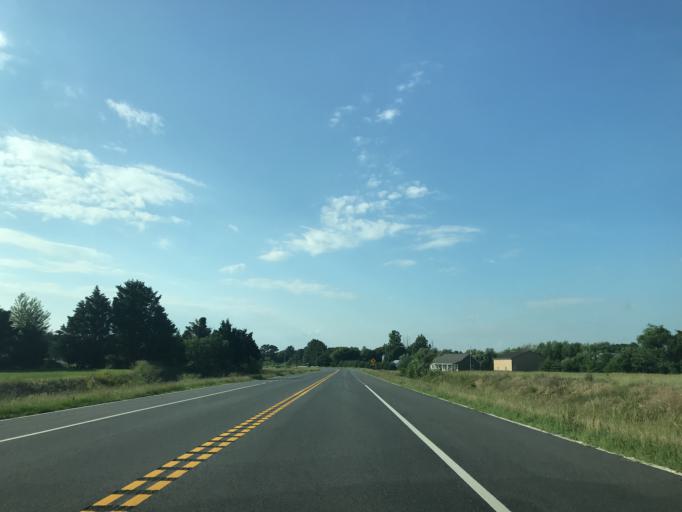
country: US
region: Maryland
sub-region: Wicomico County
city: Hebron
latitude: 38.5370
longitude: -75.7114
